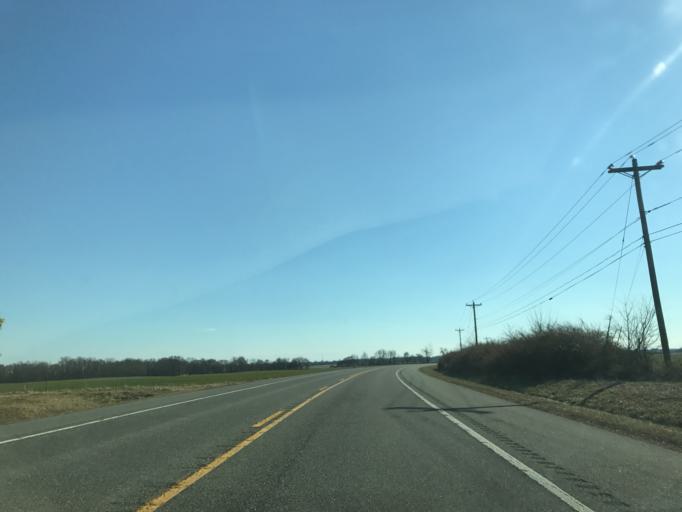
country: US
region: Maryland
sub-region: Queen Anne's County
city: Centreville
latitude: 38.9776
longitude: -76.0698
